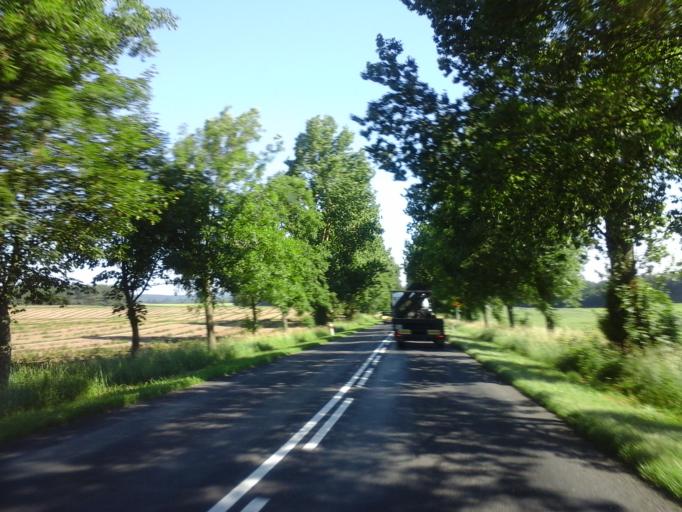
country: PL
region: West Pomeranian Voivodeship
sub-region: Powiat swidwinski
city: Polczyn-Zdroj
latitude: 53.8158
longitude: 16.0757
